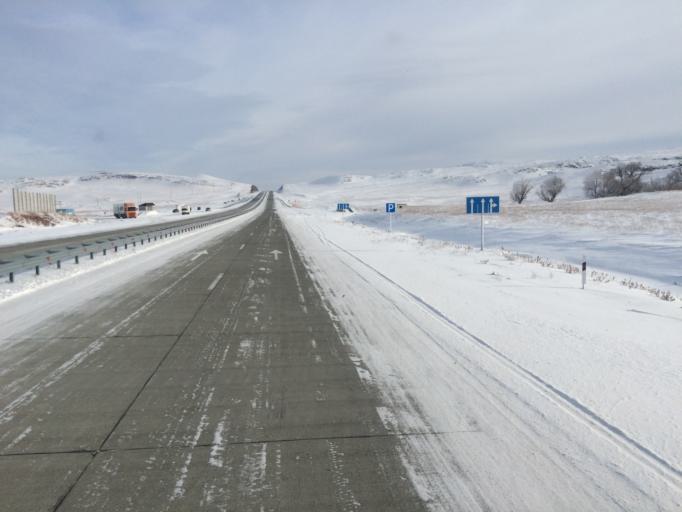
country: KZ
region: Zhambyl
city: Georgiyevka
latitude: 43.4333
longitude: 74.9327
